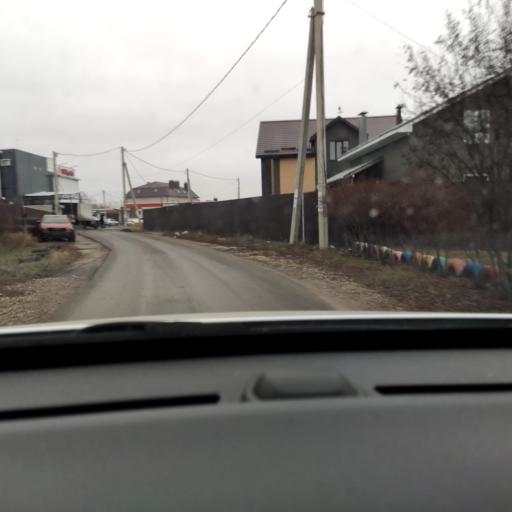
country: RU
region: Voronezj
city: Somovo
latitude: 51.6884
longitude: 39.3618
